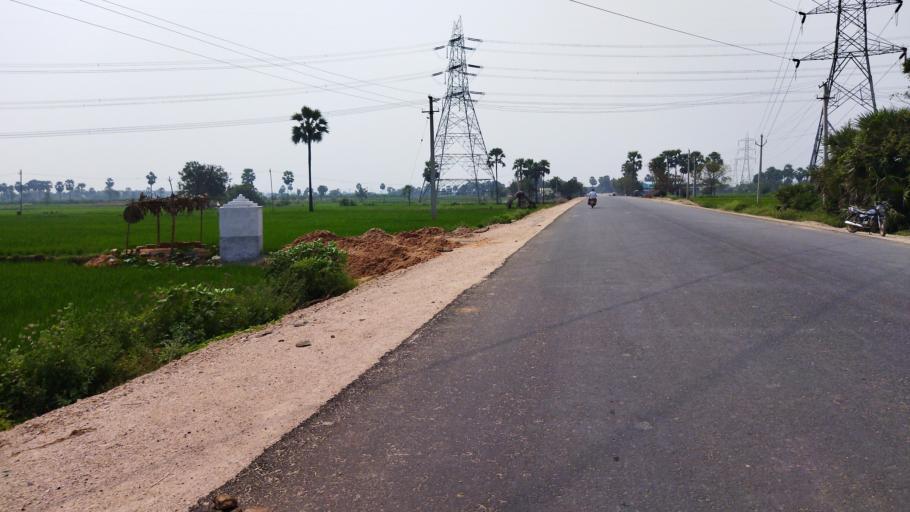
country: IN
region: Telangana
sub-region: Nalgonda
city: Nalgonda
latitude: 17.1305
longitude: 79.3746
